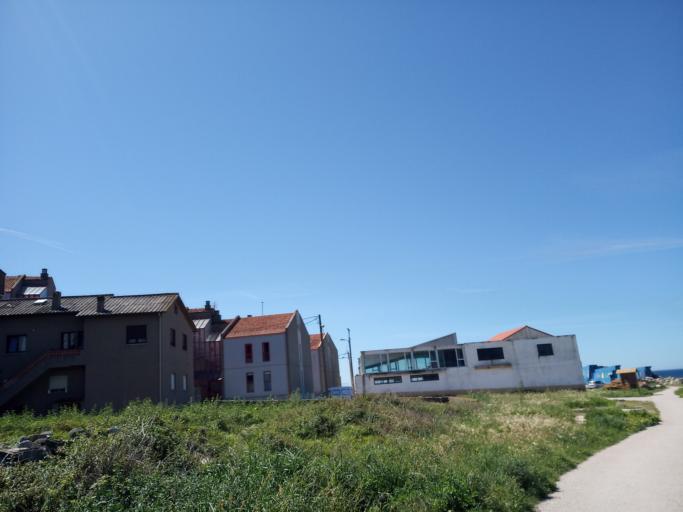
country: ES
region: Galicia
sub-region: Provincia de Pontevedra
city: A Guarda
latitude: 41.9040
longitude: -8.8793
